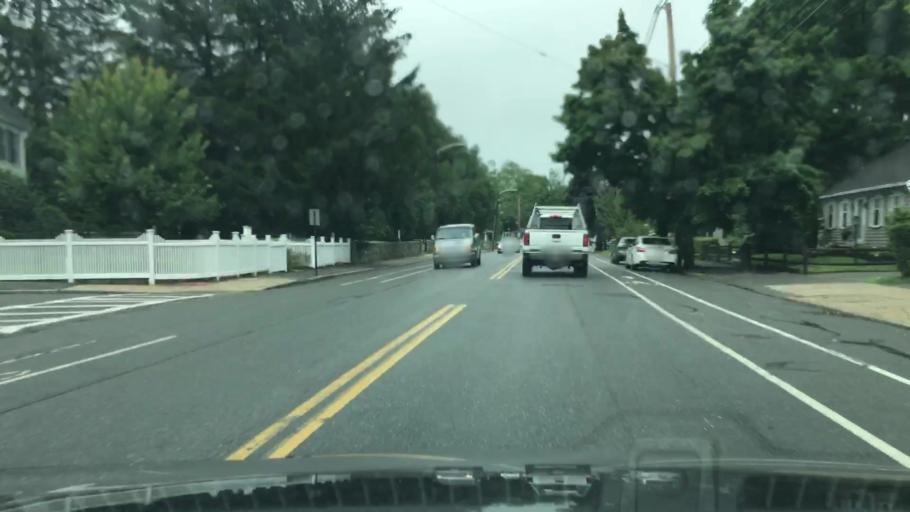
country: US
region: Massachusetts
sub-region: Essex County
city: Newburyport
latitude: 42.8131
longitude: -70.8844
